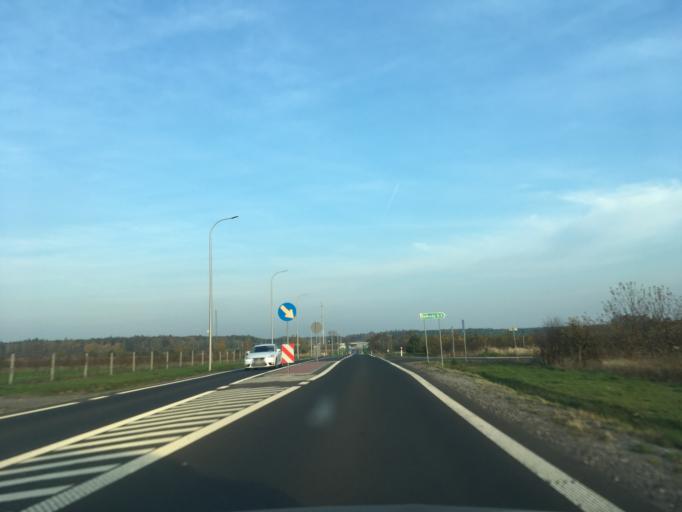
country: PL
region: Lodz Voivodeship
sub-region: Powiat skierniewicki
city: Kowiesy
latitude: 51.9200
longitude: 20.4424
